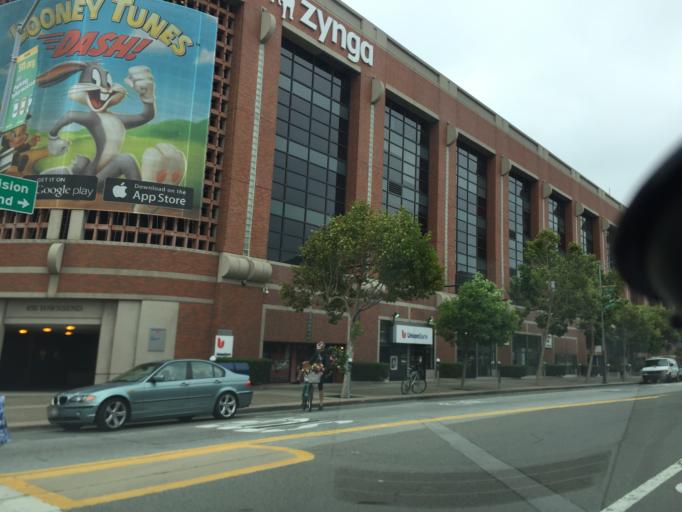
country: US
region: California
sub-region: San Francisco County
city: San Francisco
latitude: 37.7704
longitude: -122.4038
